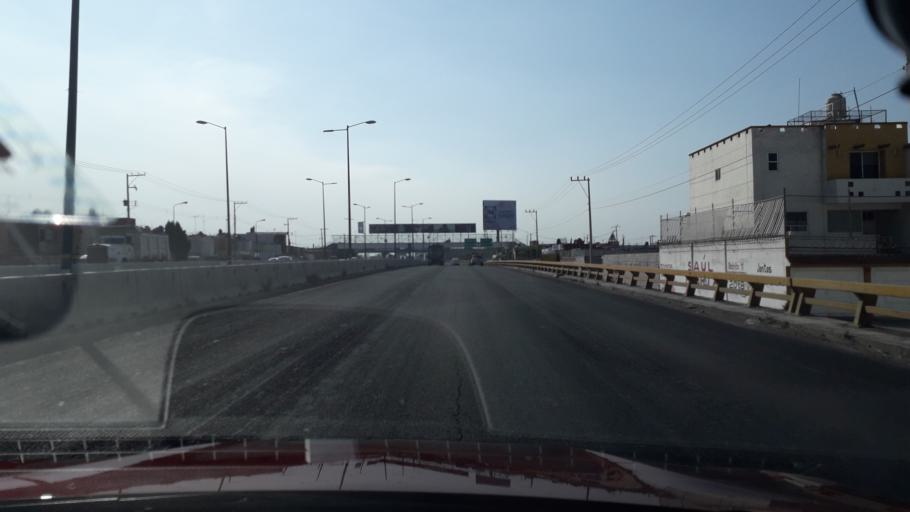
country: MX
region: Puebla
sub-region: Puebla
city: El Capulo (La Quebradora)
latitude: 18.9833
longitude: -98.2283
